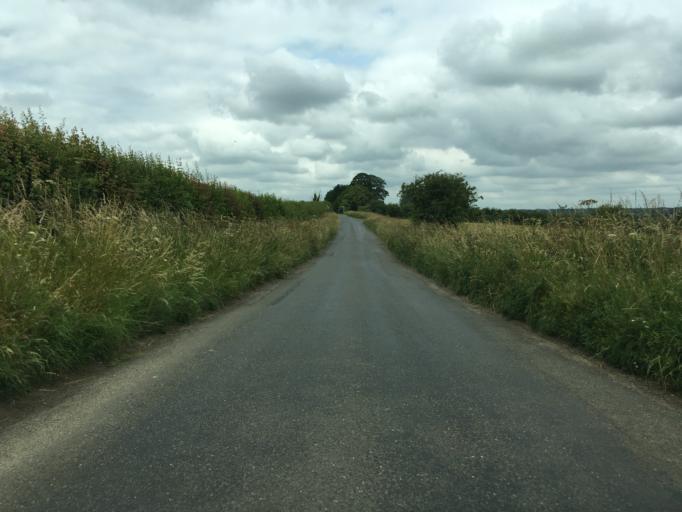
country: GB
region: England
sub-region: Oxfordshire
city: Charlbury
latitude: 51.9177
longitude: -1.4797
